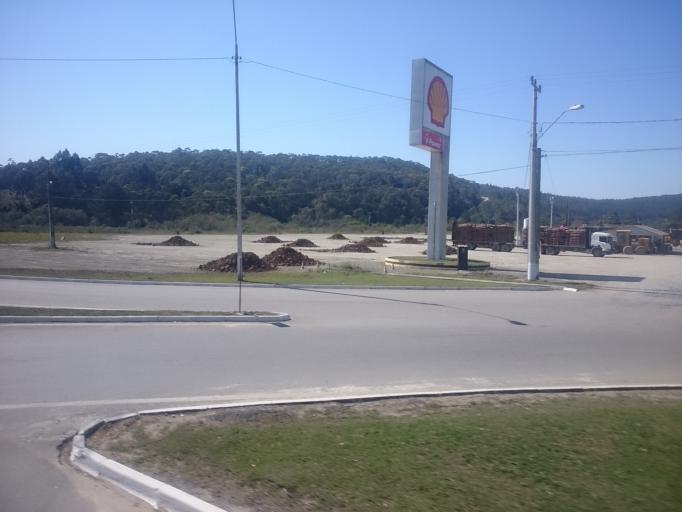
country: BR
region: Santa Catarina
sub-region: Santa Cecilia
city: Santa Cecilia
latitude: -26.7043
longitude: -50.2924
